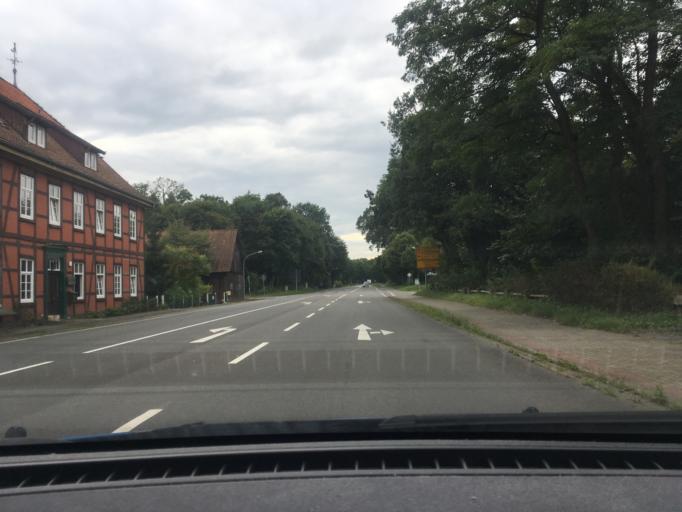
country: DE
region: Lower Saxony
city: Unterluss
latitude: 52.7926
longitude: 10.3863
